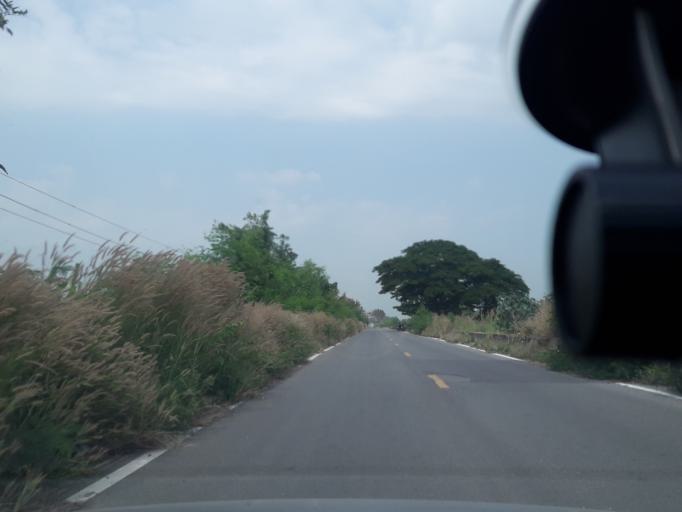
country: TH
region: Sara Buri
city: Nong Khae
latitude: 14.2651
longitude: 100.8913
